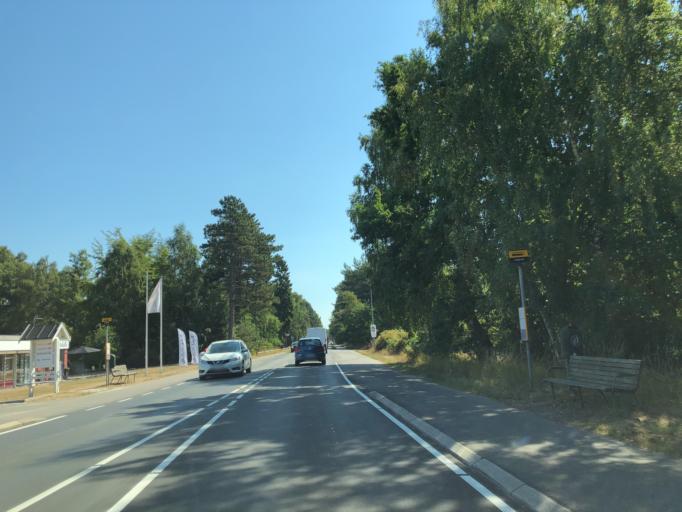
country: DK
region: Zealand
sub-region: Odsherred Kommune
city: Nykobing Sjaelland
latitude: 55.9380
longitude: 11.7043
